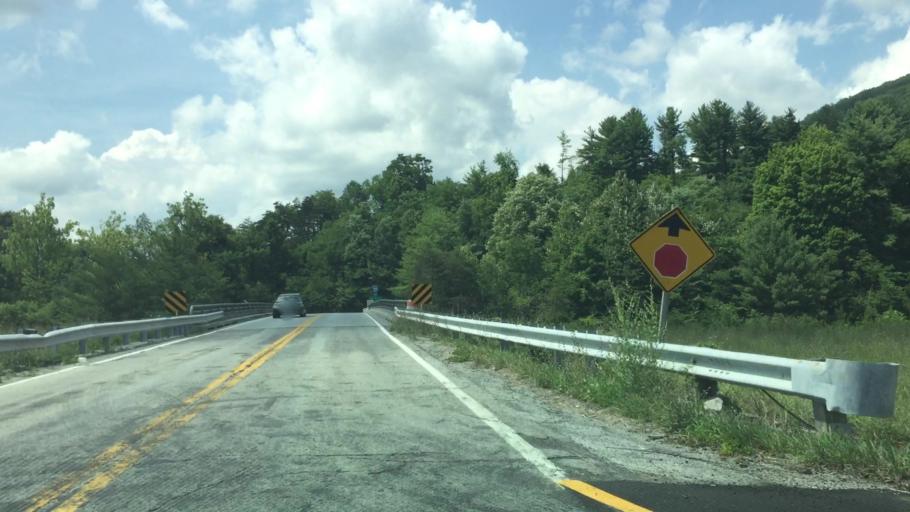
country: US
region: Virginia
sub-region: Pulaski County
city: Pulaski
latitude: 37.0068
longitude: -80.7518
